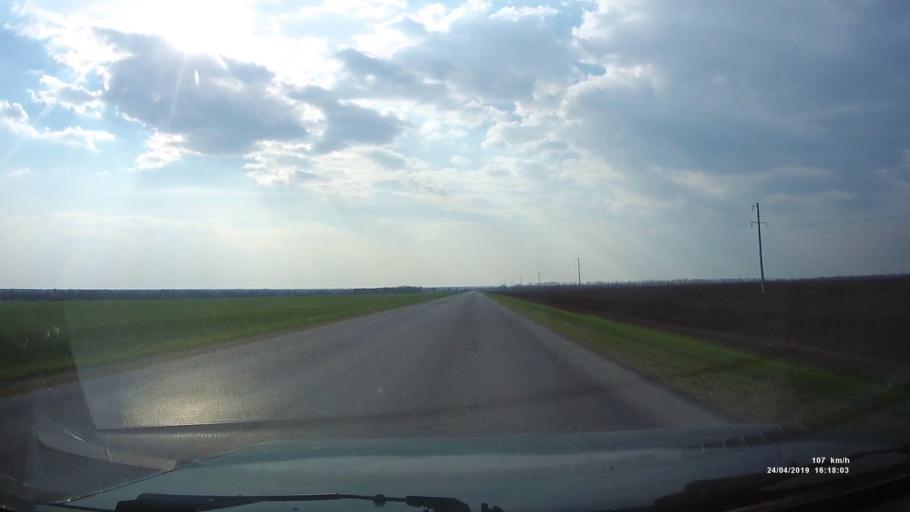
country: RU
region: Rostov
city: Sovetskoye
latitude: 46.7723
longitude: 42.1246
